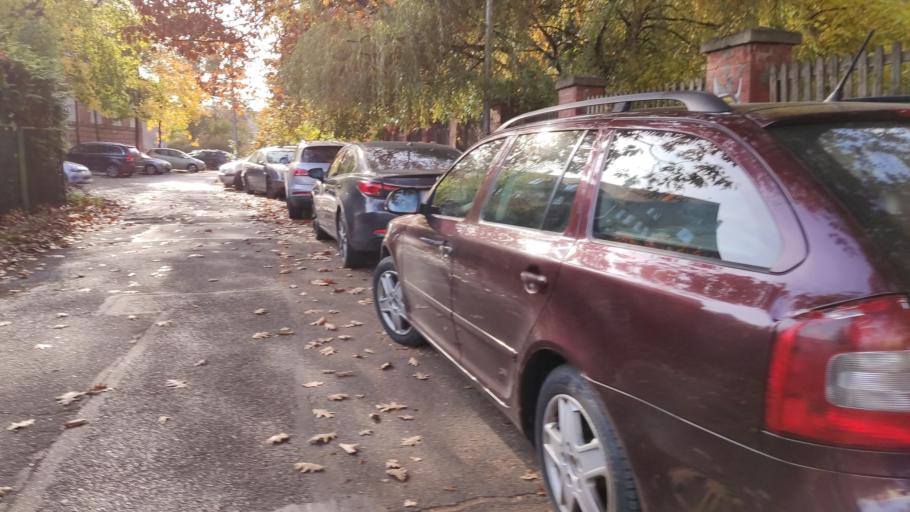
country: PL
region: Lower Silesian Voivodeship
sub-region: Powiat wroclawski
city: Wroclaw
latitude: 51.0862
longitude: 17.0199
